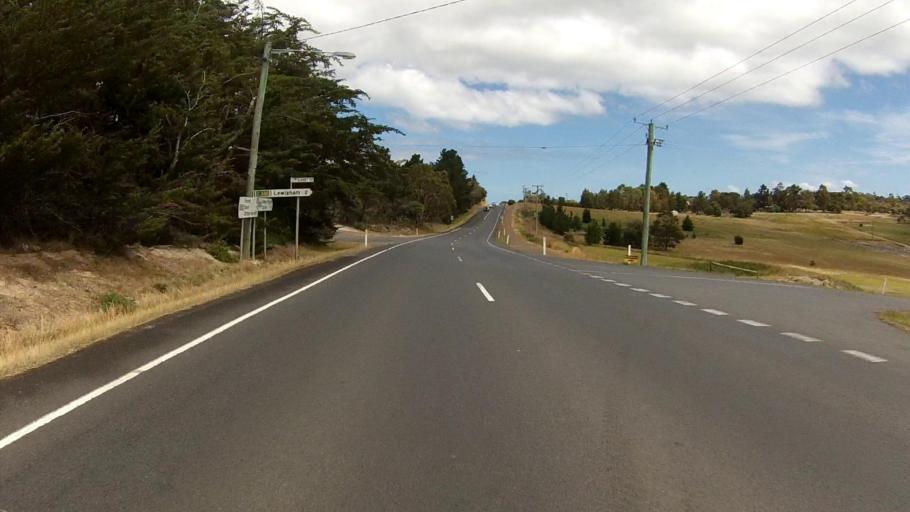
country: AU
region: Tasmania
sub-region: Sorell
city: Sorell
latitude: -42.8206
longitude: 147.6243
